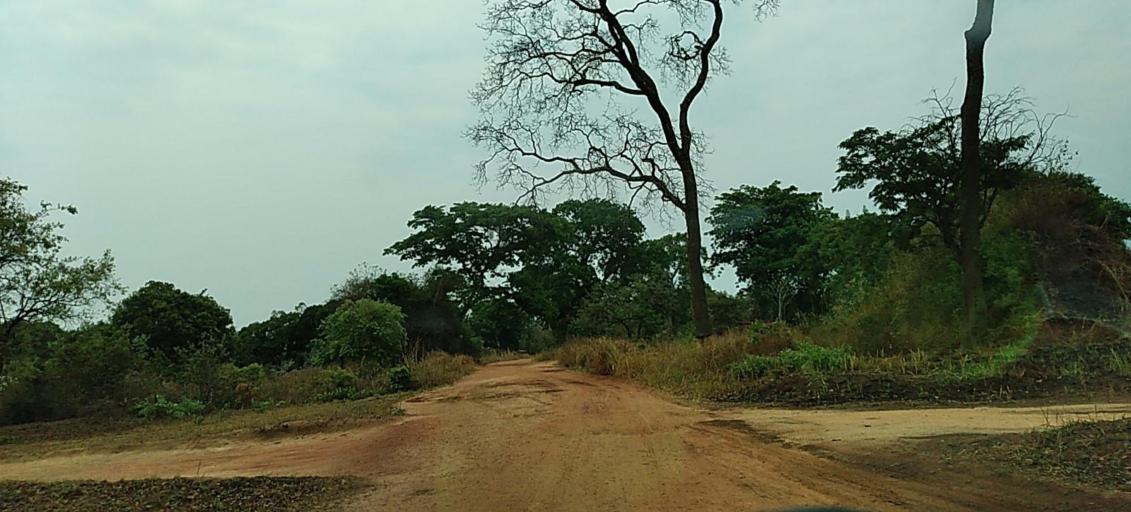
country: ZM
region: North-Western
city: Solwezi
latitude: -12.3447
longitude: 26.5290
